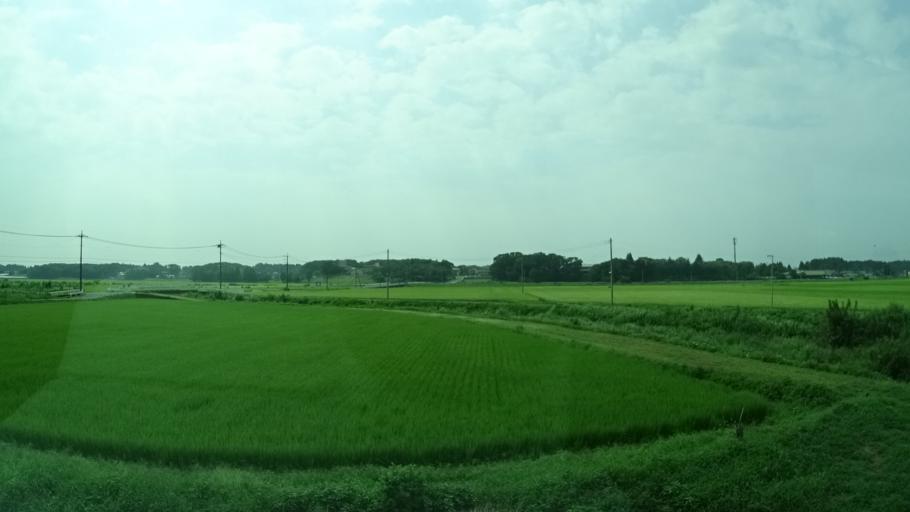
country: JP
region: Tochigi
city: Mashiko
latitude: 36.4891
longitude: 140.0939
